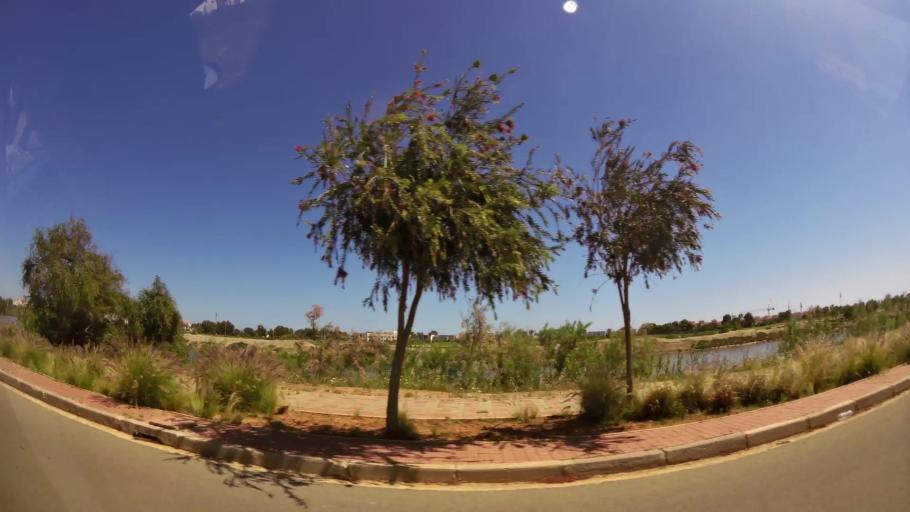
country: MA
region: Oriental
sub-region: Berkane-Taourirt
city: Madagh
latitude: 35.1046
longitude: -2.3101
